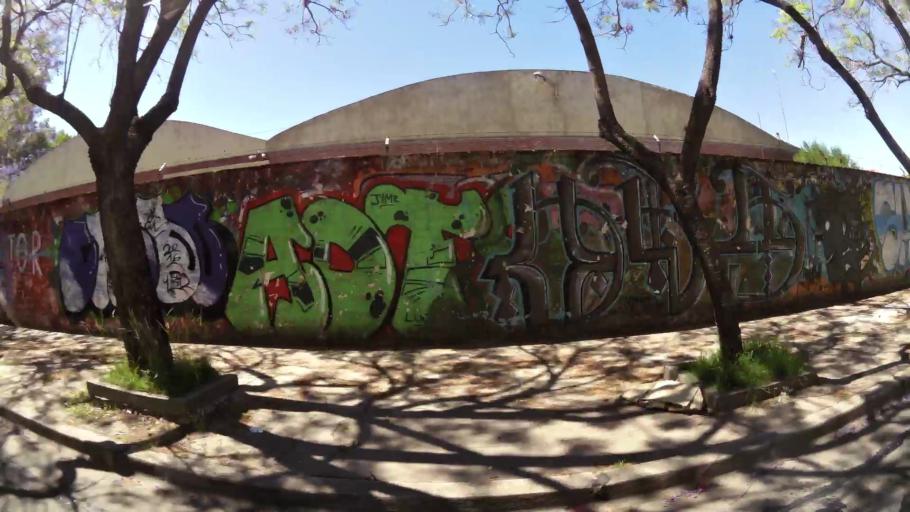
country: AR
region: Buenos Aires
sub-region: Partido de General San Martin
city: General San Martin
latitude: -34.5308
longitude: -58.5425
